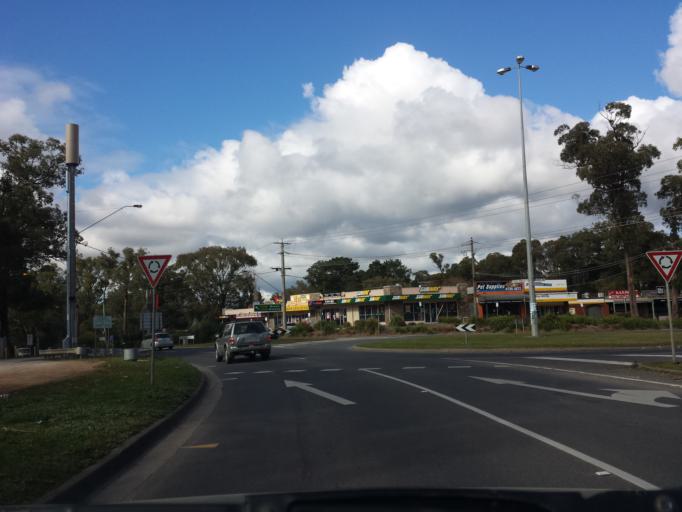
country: AU
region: Victoria
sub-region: Yarra Ranges
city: Mount Evelyn
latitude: -37.7856
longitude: 145.3819
